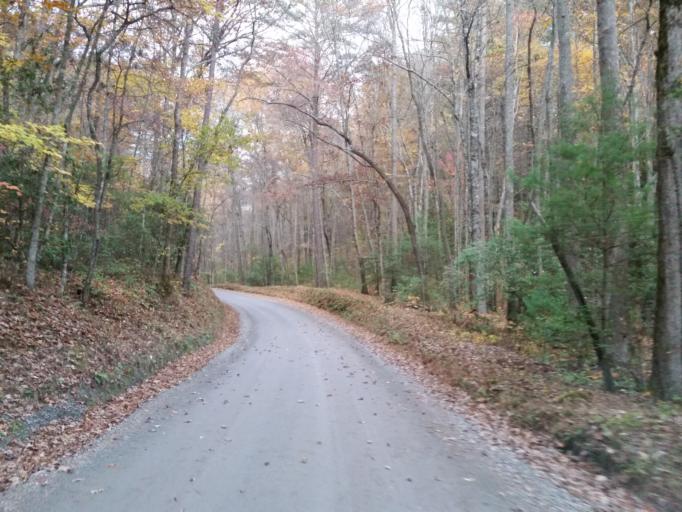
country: US
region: Georgia
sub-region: Fannin County
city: Blue Ridge
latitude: 34.7255
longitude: -84.2106
